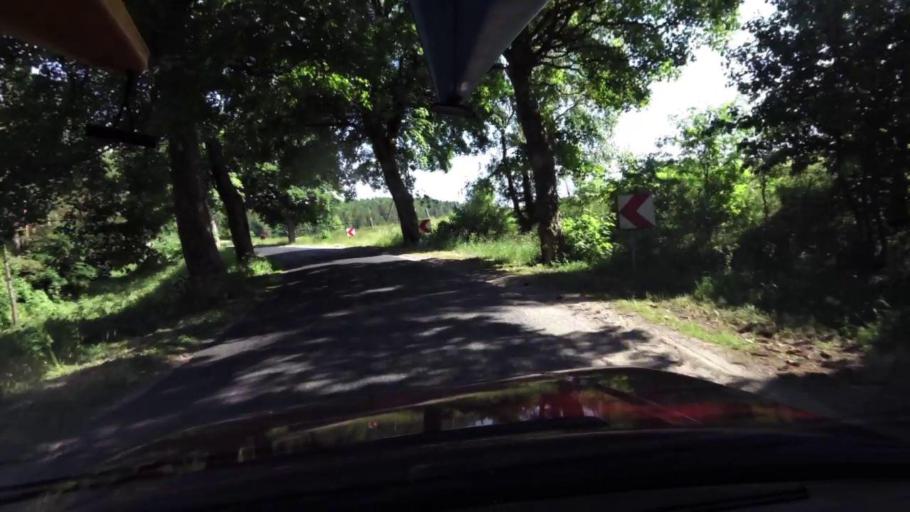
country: PL
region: Pomeranian Voivodeship
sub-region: Powiat slupski
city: Kepice
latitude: 54.1298
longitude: 16.9319
